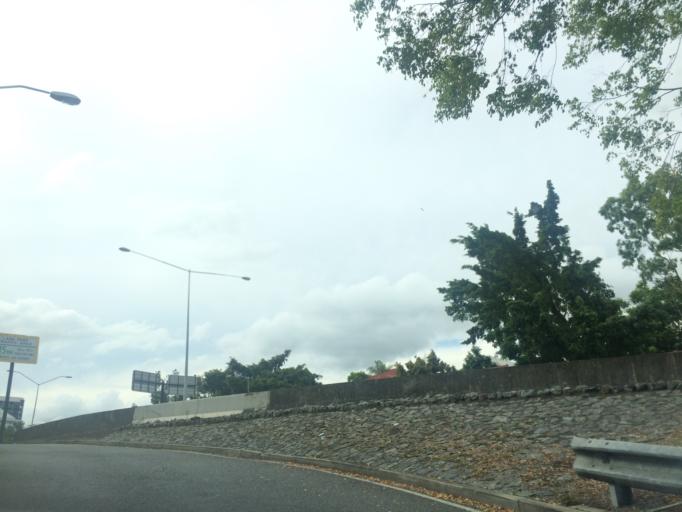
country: AU
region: Queensland
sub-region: Brisbane
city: Spring Hill
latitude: -27.4581
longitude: 153.0148
